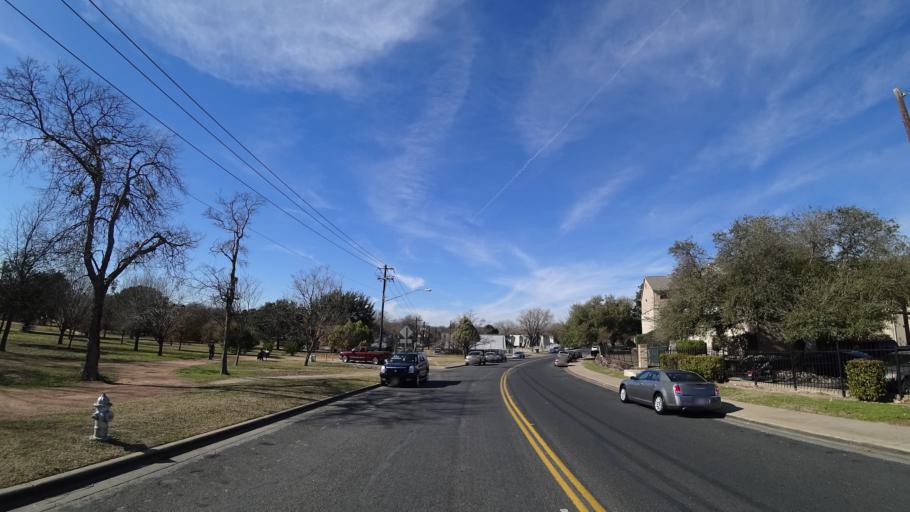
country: US
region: Texas
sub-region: Travis County
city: Wells Branch
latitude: 30.3700
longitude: -97.7013
